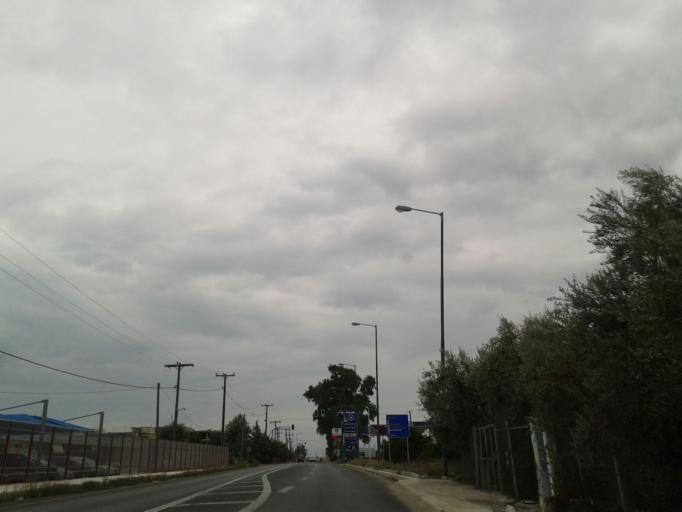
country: GR
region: Peloponnese
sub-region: Nomos Argolidos
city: Argos
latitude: 37.6530
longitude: 22.7279
